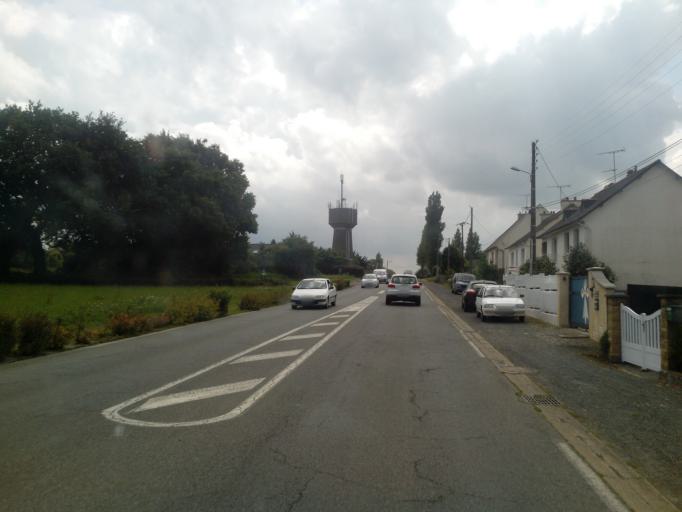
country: FR
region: Brittany
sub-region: Departement des Cotes-d'Armor
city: Plouha
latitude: 48.6804
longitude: -2.9310
